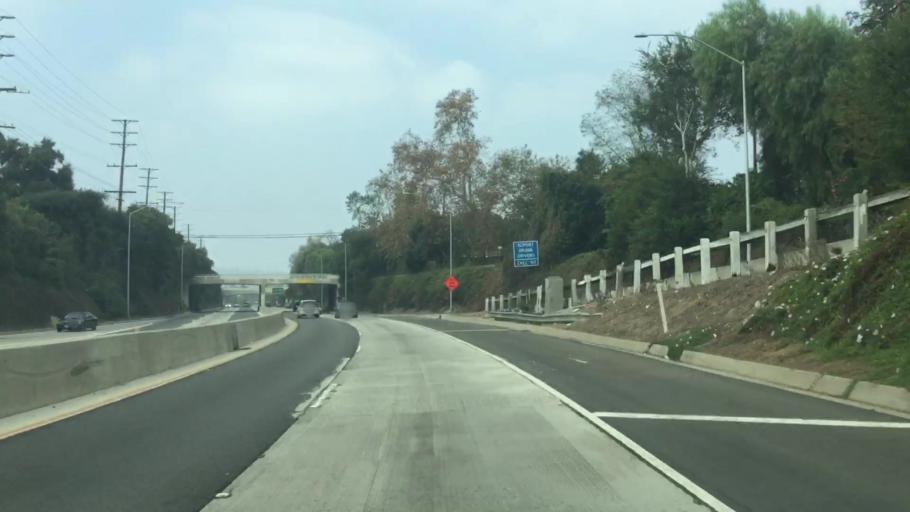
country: US
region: California
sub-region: Los Angeles County
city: South Pasadena
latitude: 34.1193
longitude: -118.1616
